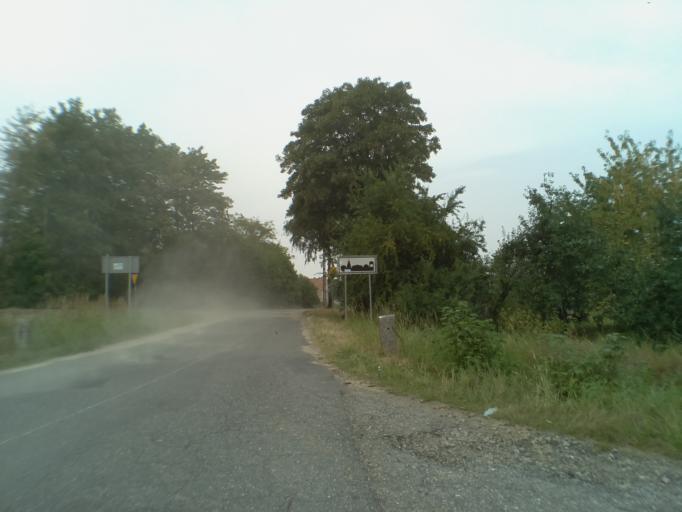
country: PL
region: Lower Silesian Voivodeship
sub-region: Powiat swidnicki
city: Strzegom
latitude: 50.9755
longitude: 16.3075
